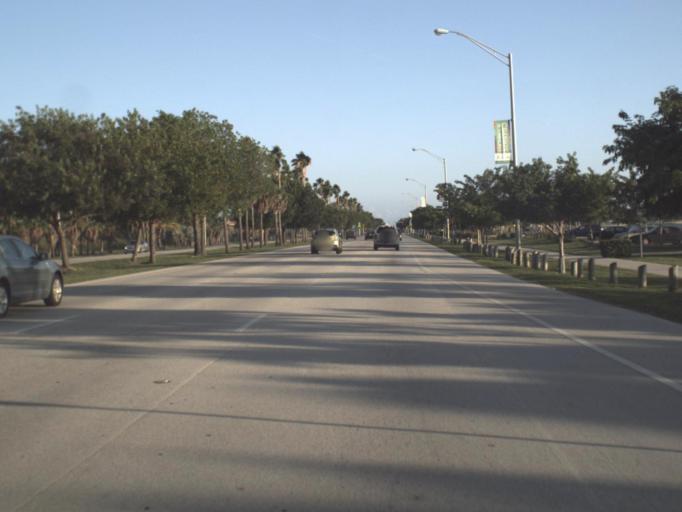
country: US
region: Florida
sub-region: Miami-Dade County
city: Miami
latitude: 25.7410
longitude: -80.1708
